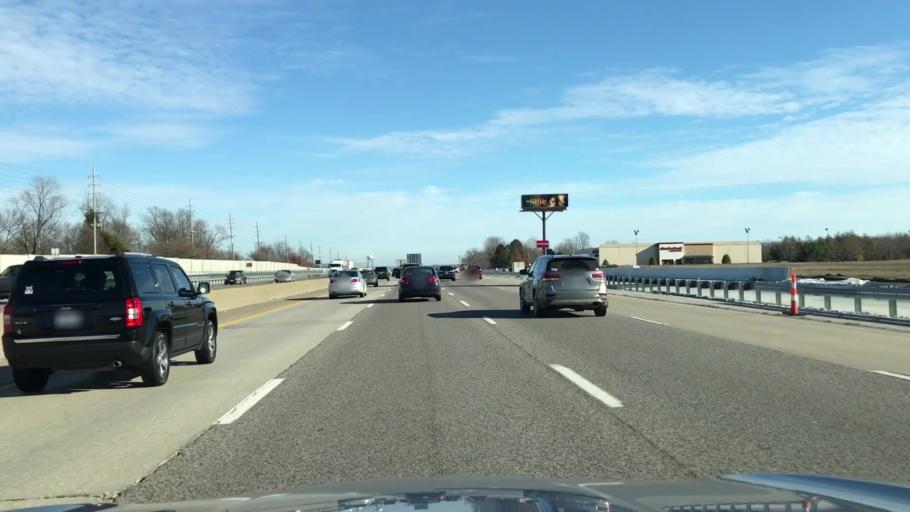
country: US
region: Missouri
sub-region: Saint Charles County
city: O'Fallon
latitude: 38.8026
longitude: -90.6927
